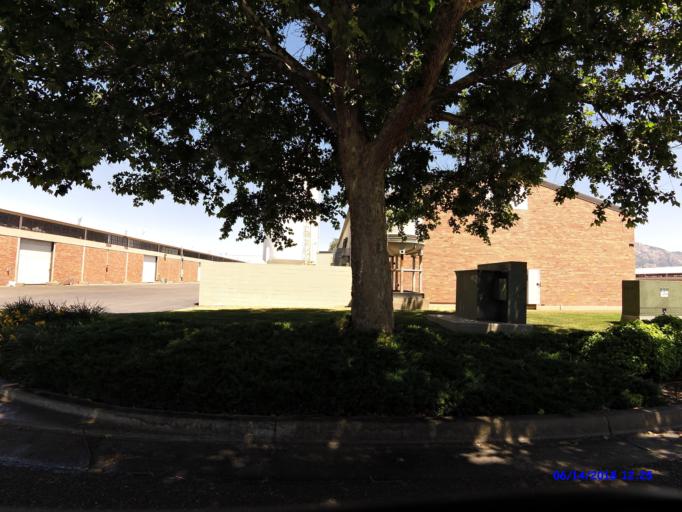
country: US
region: Utah
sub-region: Weber County
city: Harrisville
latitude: 41.2594
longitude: -111.9957
